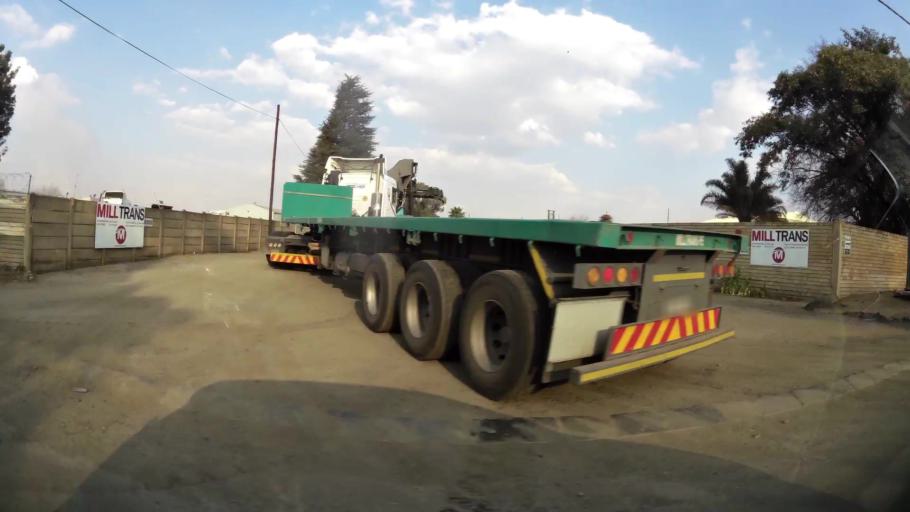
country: ZA
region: Gauteng
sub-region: Ekurhuleni Metropolitan Municipality
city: Benoni
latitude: -26.1105
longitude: 28.2696
